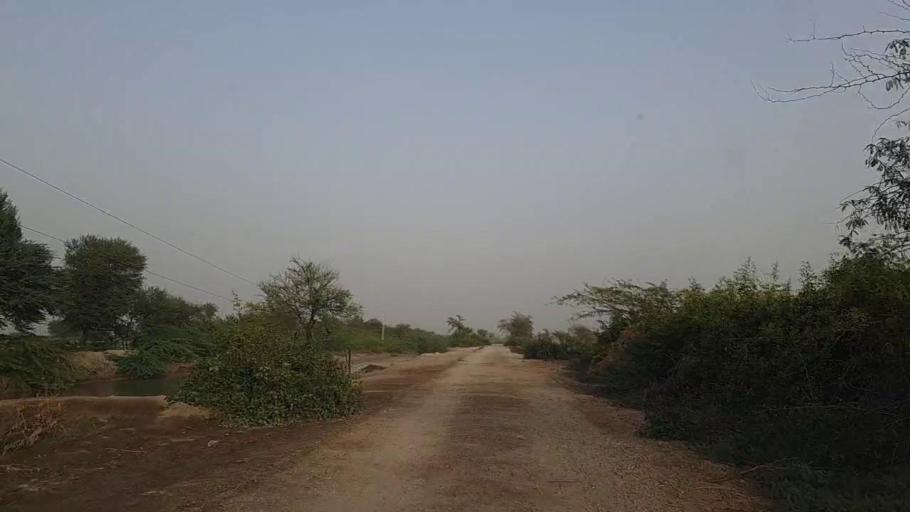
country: PK
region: Sindh
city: Pithoro
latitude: 25.4506
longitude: 69.4260
